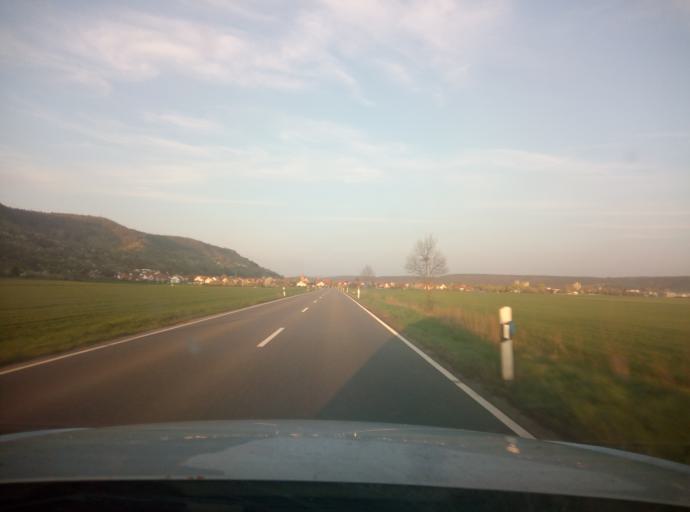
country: DE
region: Baden-Wuerttemberg
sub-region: Tuebingen Region
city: Rottenburg
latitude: 48.5009
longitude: 8.9800
